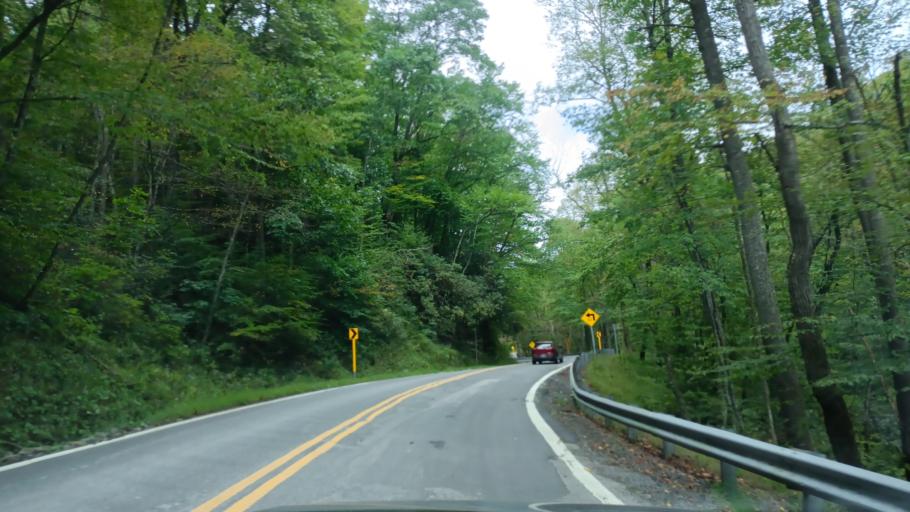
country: US
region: West Virginia
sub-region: Preston County
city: Kingwood
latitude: 39.3275
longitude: -79.7233
